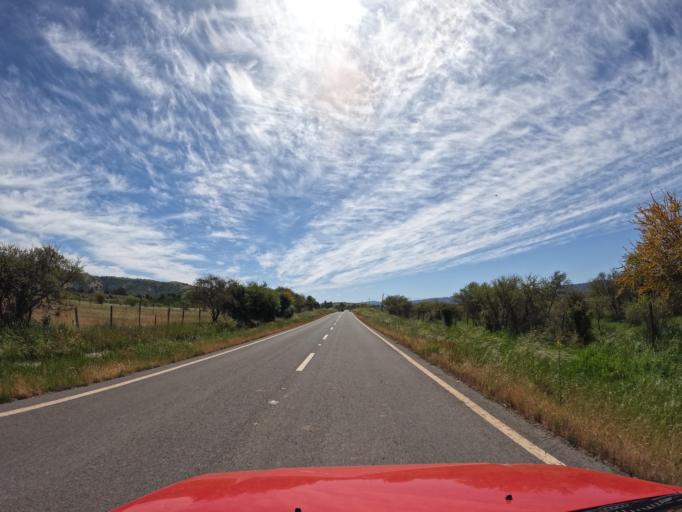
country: CL
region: Maule
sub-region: Provincia de Talca
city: Talca
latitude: -35.0345
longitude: -71.7594
